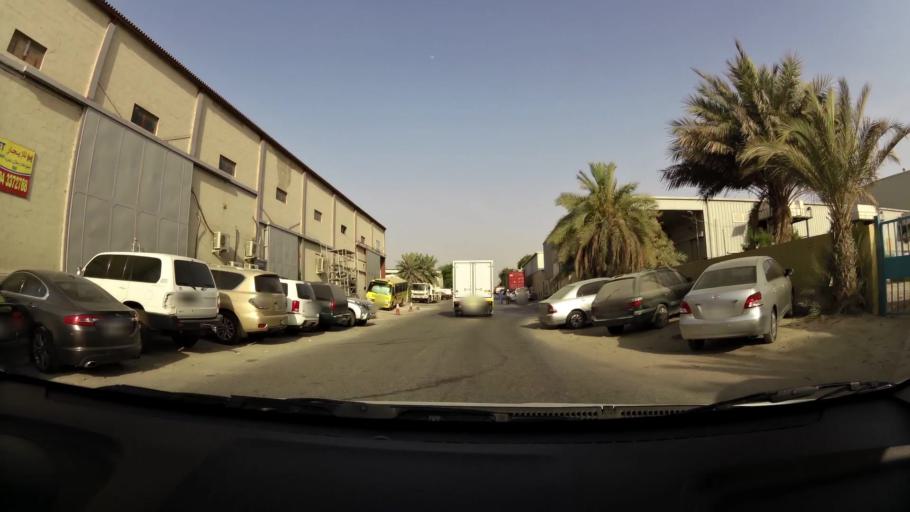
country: AE
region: Ash Shariqah
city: Sharjah
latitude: 25.2268
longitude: 55.3625
